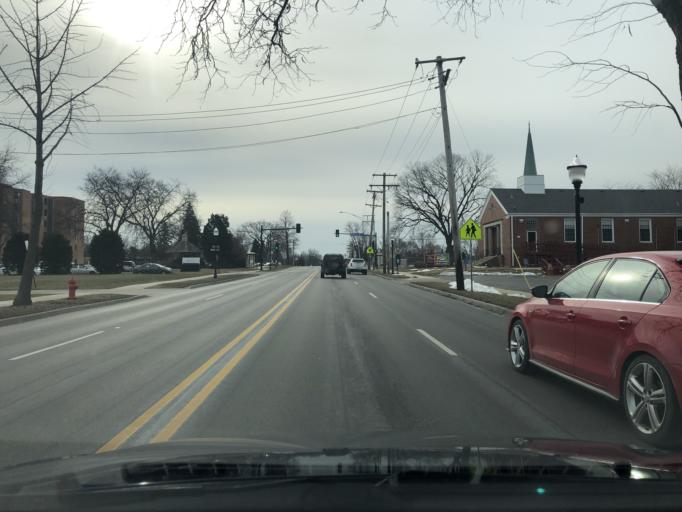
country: US
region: Illinois
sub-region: DuPage County
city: Bensenville
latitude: 41.9511
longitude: -87.9397
